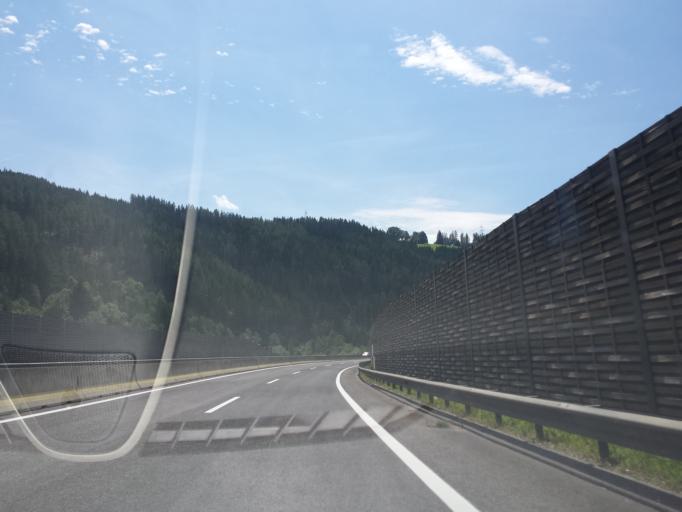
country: AT
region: Styria
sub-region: Politischer Bezirk Bruck-Muerzzuschlag
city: Spital am Semmering
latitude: 47.6037
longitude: 15.7312
